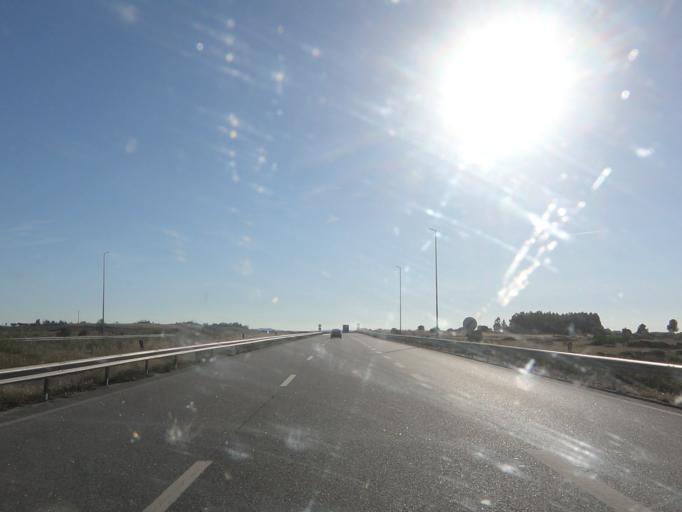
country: ES
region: Castille and Leon
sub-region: Provincia de Salamanca
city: Fuentes de Onoro
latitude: 40.6044
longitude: -6.9545
